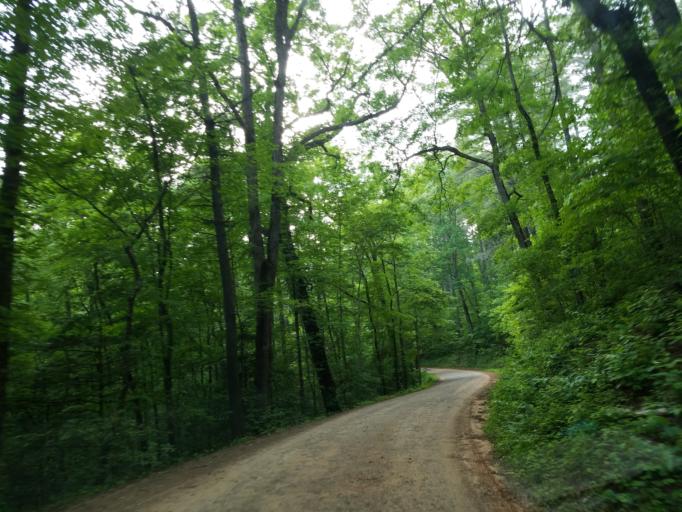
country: US
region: Georgia
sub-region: Lumpkin County
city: Dahlonega
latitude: 34.6029
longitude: -84.0974
